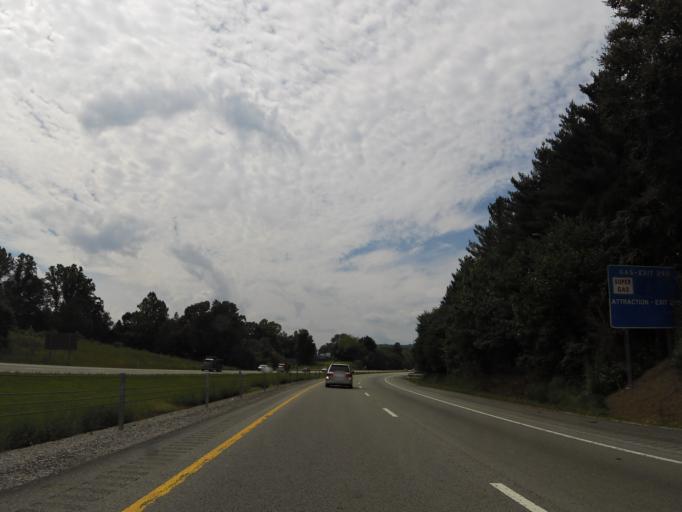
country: US
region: Tennessee
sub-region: Putnam County
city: Algood
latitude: 36.1417
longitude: -85.4207
